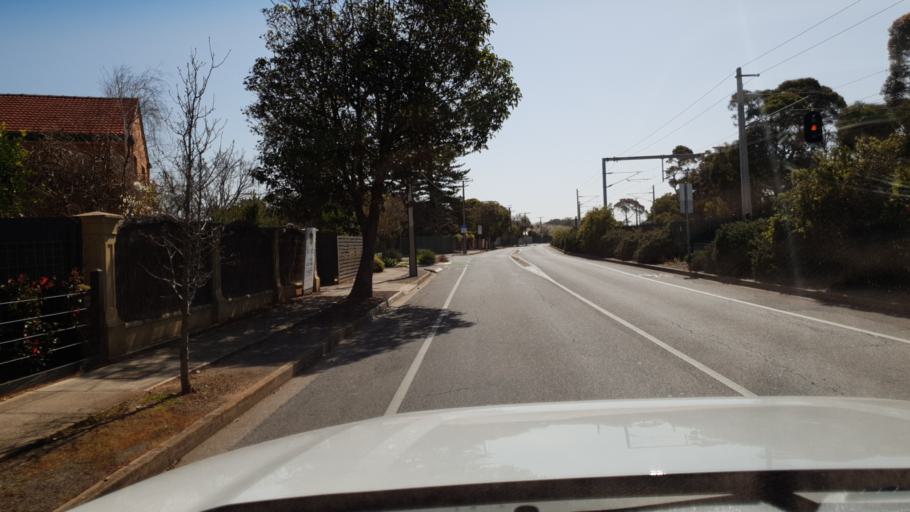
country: AU
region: South Australia
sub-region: Adelaide
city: Brighton
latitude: -35.0158
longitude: 138.5192
